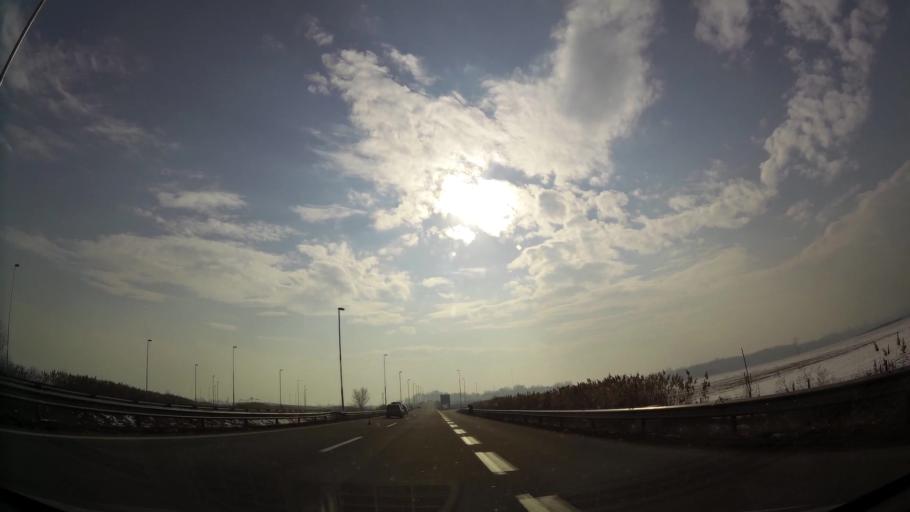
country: MK
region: Aracinovo
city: Arachinovo
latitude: 41.9995
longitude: 21.5329
